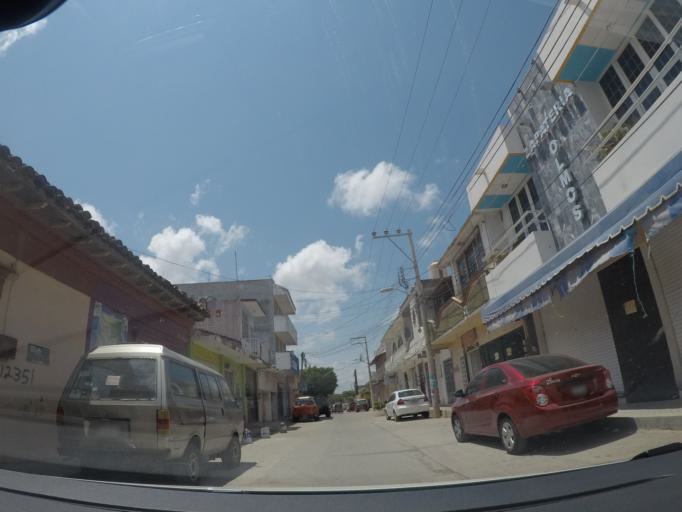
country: MX
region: Oaxaca
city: Juchitan de Zaragoza
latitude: 16.4340
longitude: -95.0198
